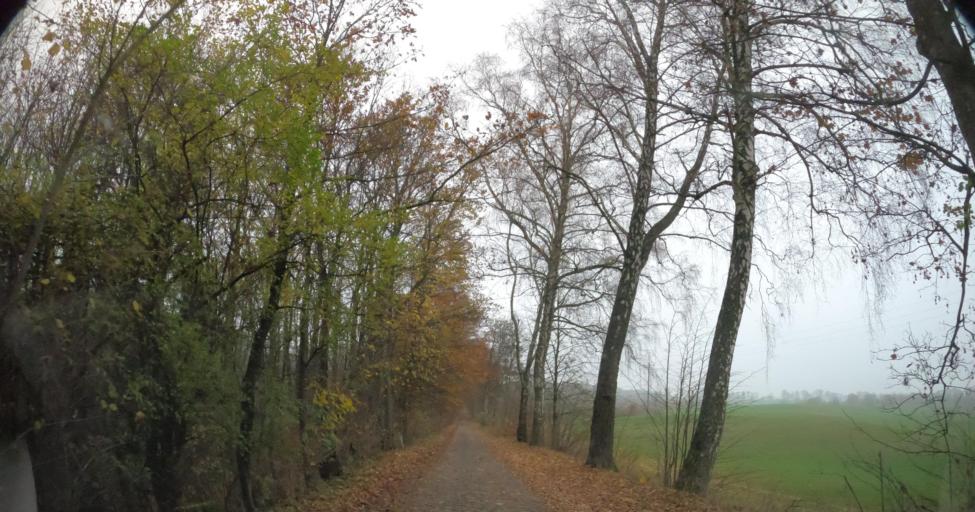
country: PL
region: West Pomeranian Voivodeship
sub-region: Powiat drawski
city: Drawsko Pomorskie
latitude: 53.5671
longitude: 15.7253
